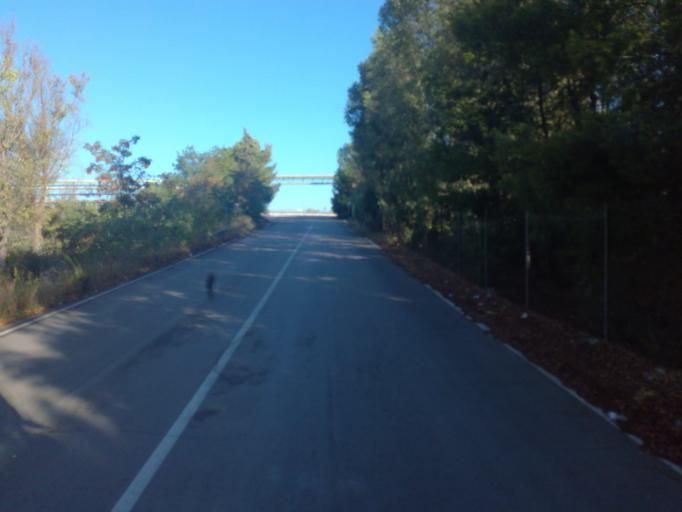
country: IT
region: Apulia
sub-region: Provincia di Taranto
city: Statte
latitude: 40.5123
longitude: 17.1840
